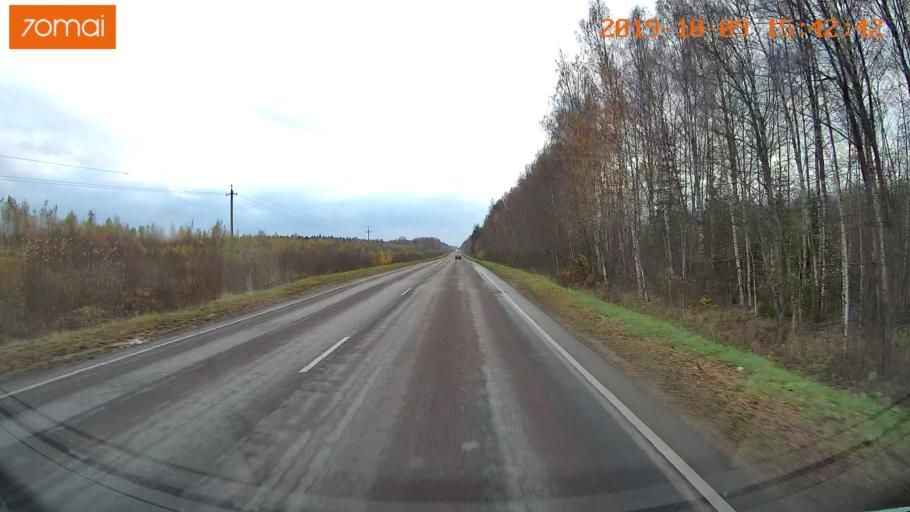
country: RU
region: Kostroma
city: Oktyabr'skiy
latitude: 57.8655
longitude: 41.1019
